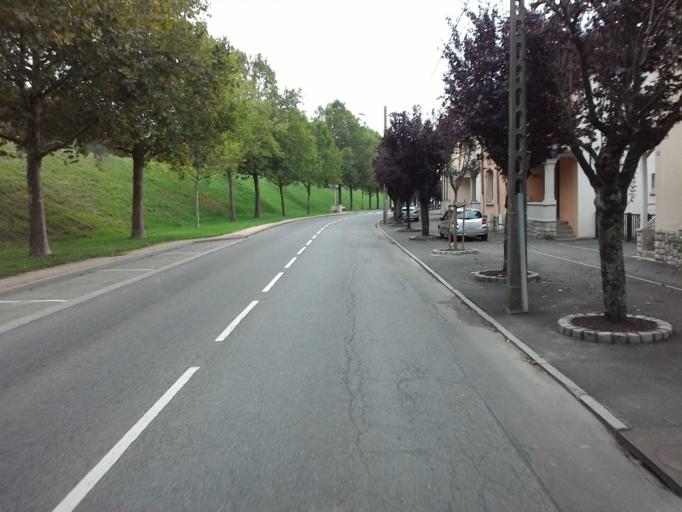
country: FR
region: Lorraine
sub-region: Departement de Meurthe-et-Moselle
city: Toul
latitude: 48.6792
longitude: 5.8961
